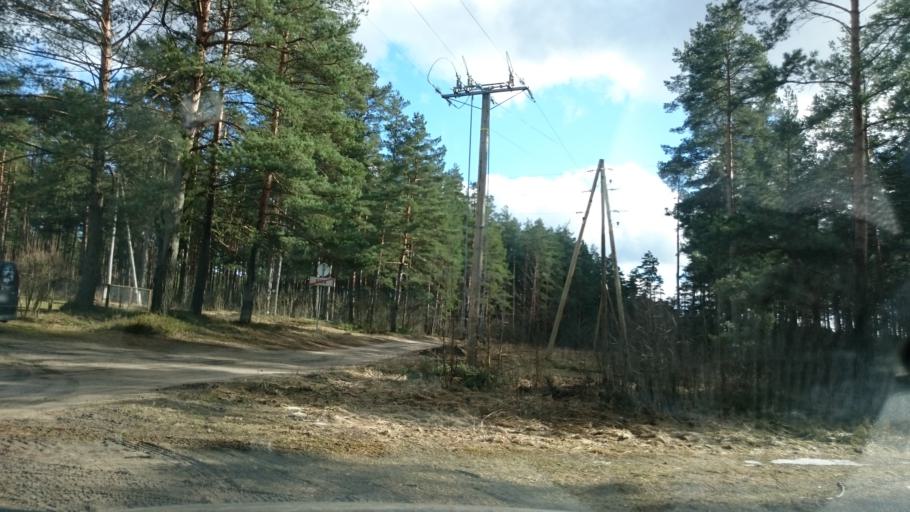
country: LV
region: Stopini
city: Ulbroka
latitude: 56.9554
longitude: 24.2868
